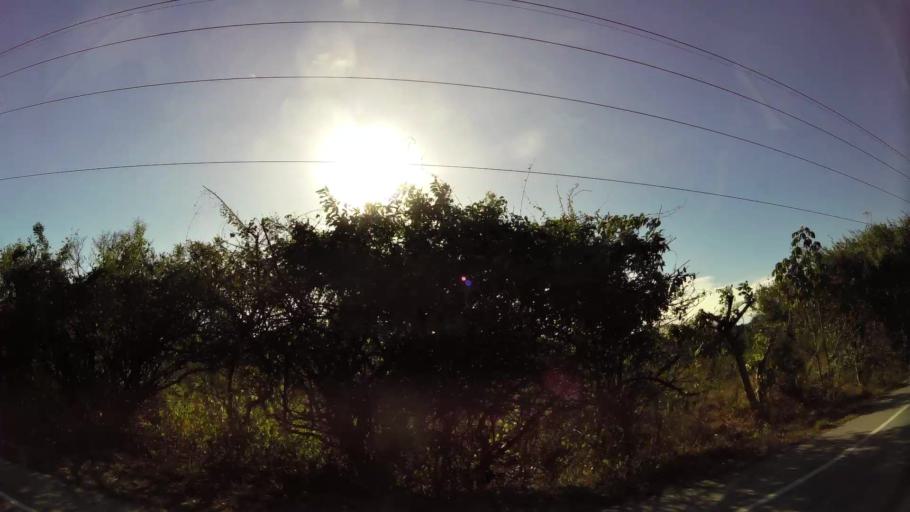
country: SV
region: Santa Ana
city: Metapan
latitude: 14.2353
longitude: -89.4682
